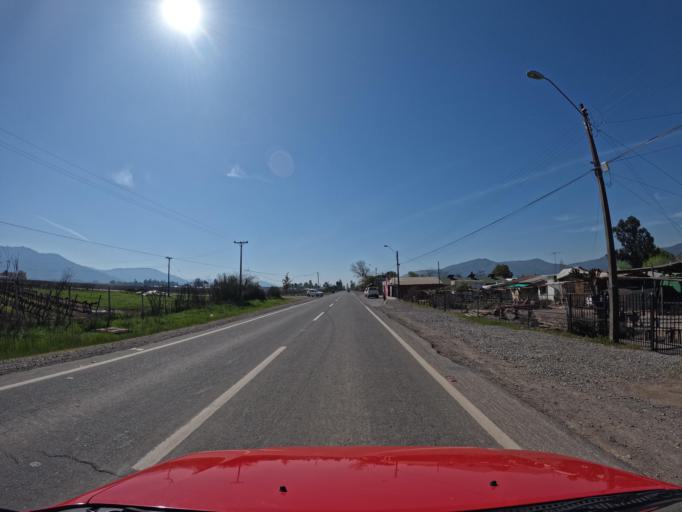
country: CL
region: Maule
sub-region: Provincia de Curico
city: Rauco
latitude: -35.0416
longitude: -71.4566
